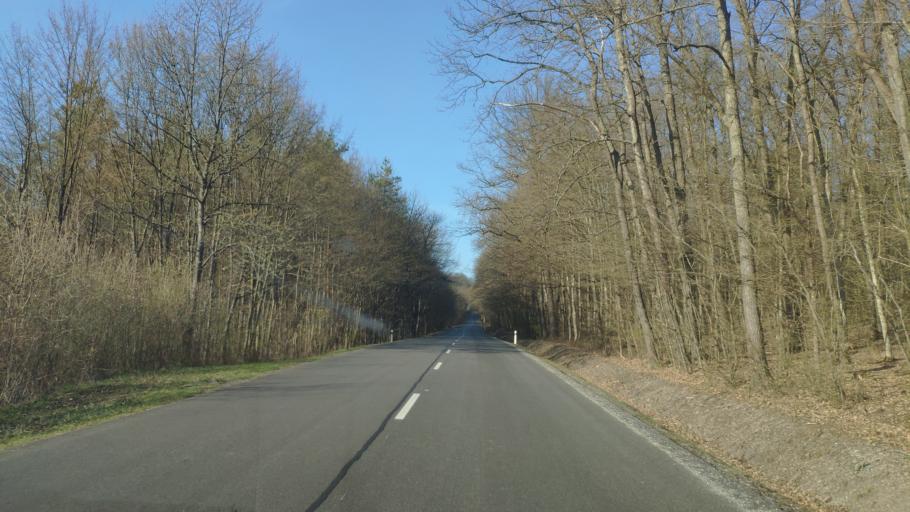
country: HU
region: Borsod-Abauj-Zemplen
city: Putnok
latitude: 48.4990
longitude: 20.2851
